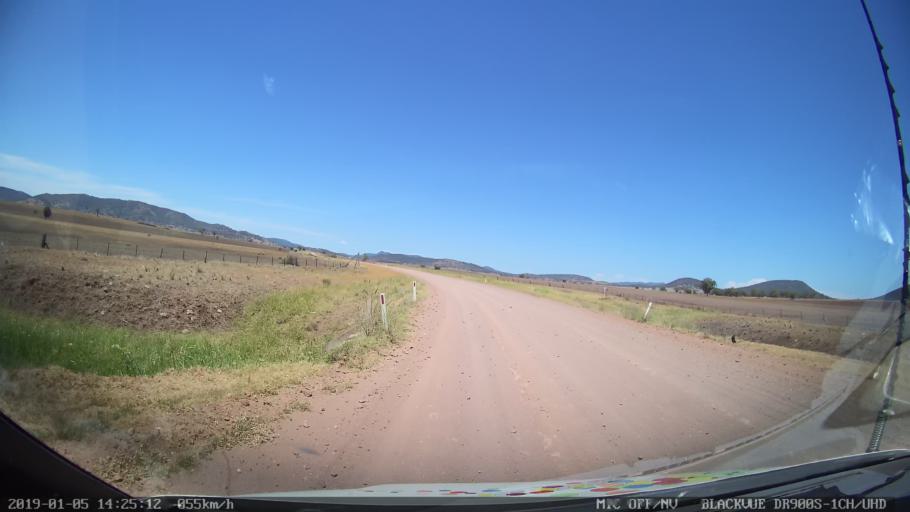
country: AU
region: New South Wales
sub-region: Liverpool Plains
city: Quirindi
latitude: -31.2417
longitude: 150.5472
